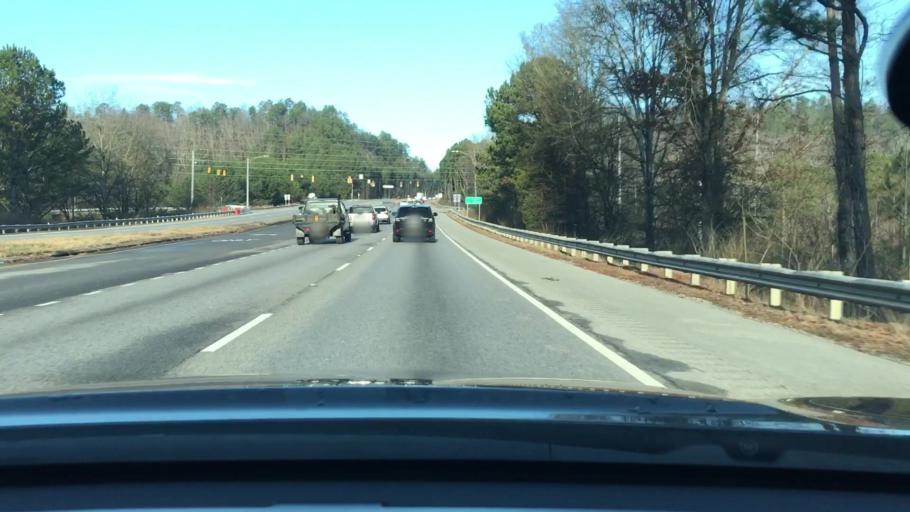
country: US
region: Alabama
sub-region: Shelby County
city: Chelsea
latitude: 33.3550
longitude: -86.6496
